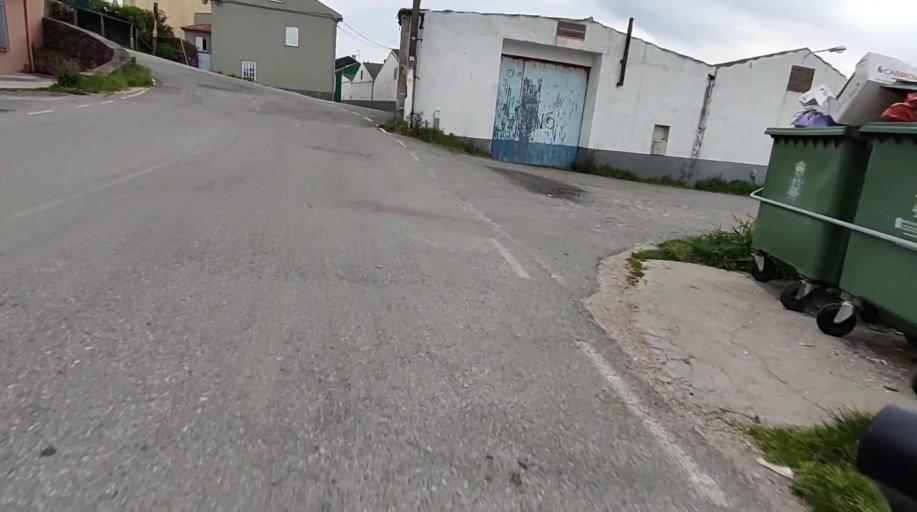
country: ES
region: Galicia
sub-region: Provincia da Coruna
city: Boiro
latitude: 42.6205
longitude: -8.8865
